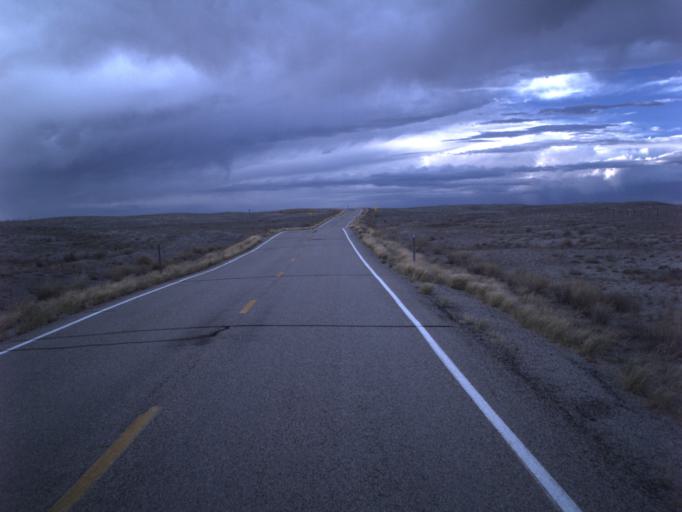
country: US
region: Utah
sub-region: Grand County
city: Moab
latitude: 38.8906
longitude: -109.3111
